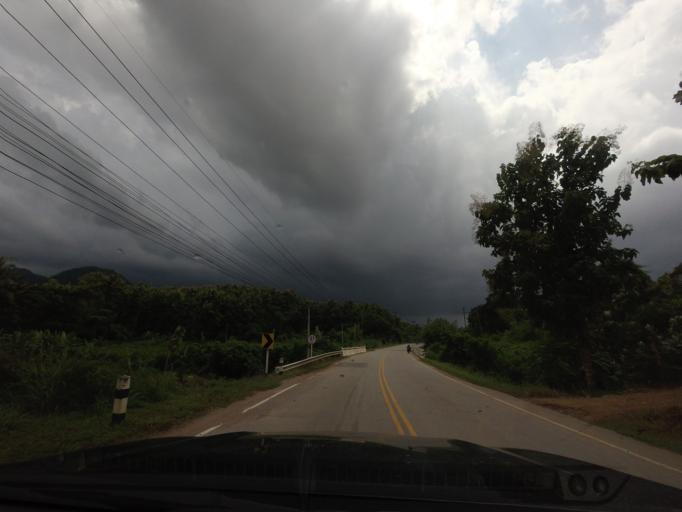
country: LA
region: Vientiane
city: Muang Sanakham
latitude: 17.9782
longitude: 101.7479
